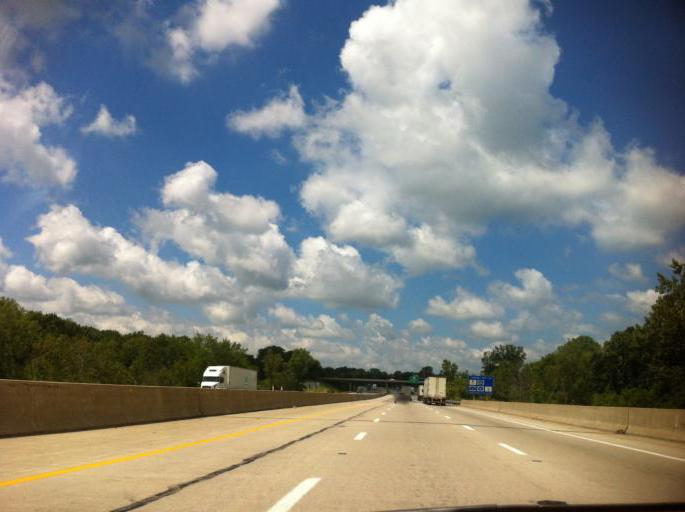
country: US
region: Ohio
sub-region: Erie County
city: Milan
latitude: 41.3238
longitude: -82.5893
